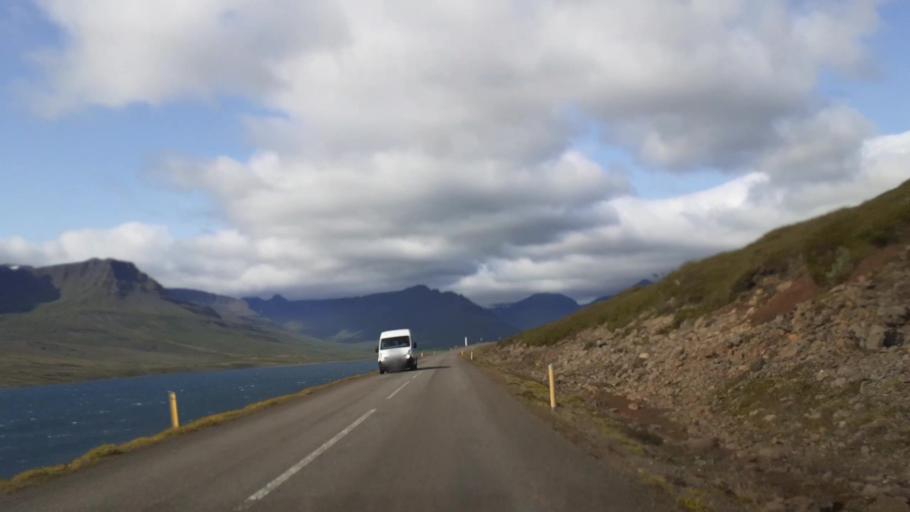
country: IS
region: East
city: Eskifjoerdur
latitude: 64.9222
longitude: -13.9694
